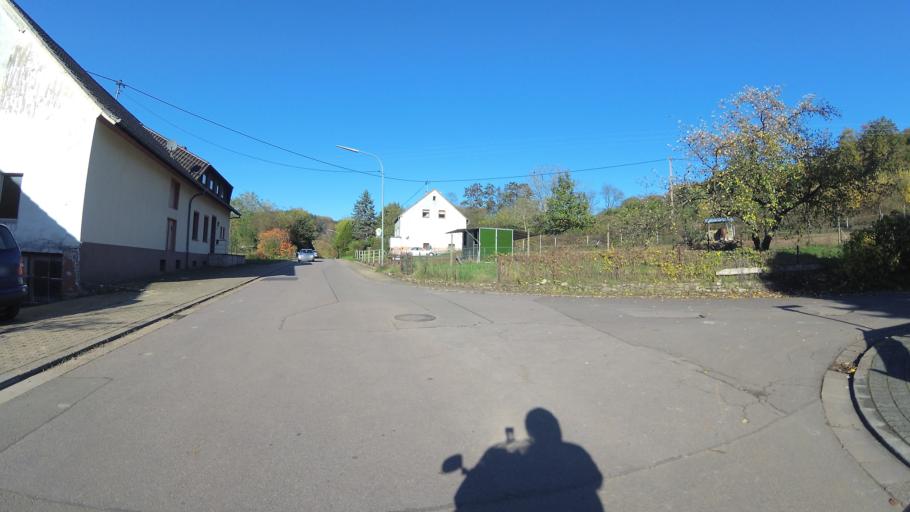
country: DE
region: Saarland
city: Losheim
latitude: 49.4629
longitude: 6.7558
